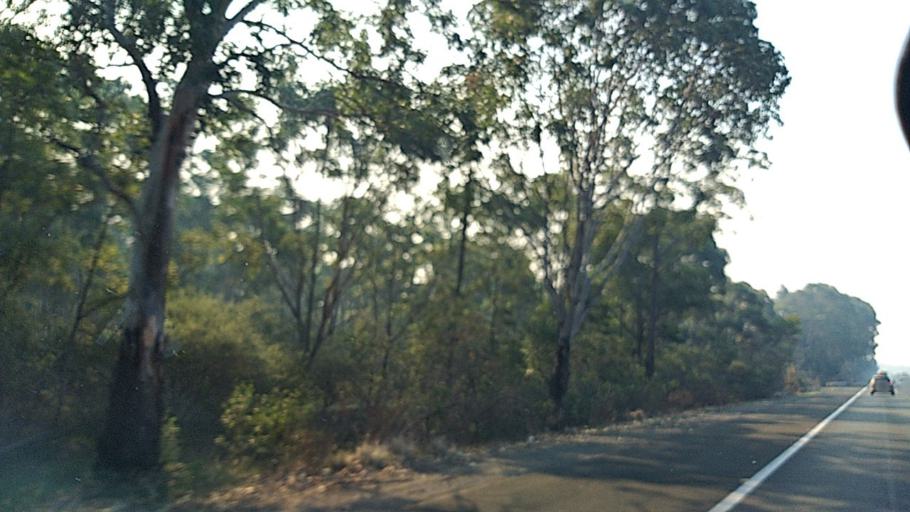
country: AU
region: New South Wales
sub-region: Wollondilly
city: Picton
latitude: -34.2675
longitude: 150.6479
